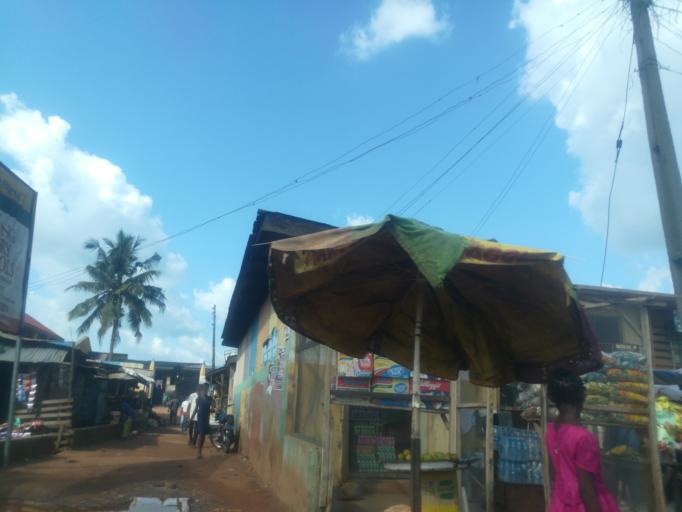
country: NG
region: Oyo
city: Ibadan
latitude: 7.4223
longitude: 3.9740
